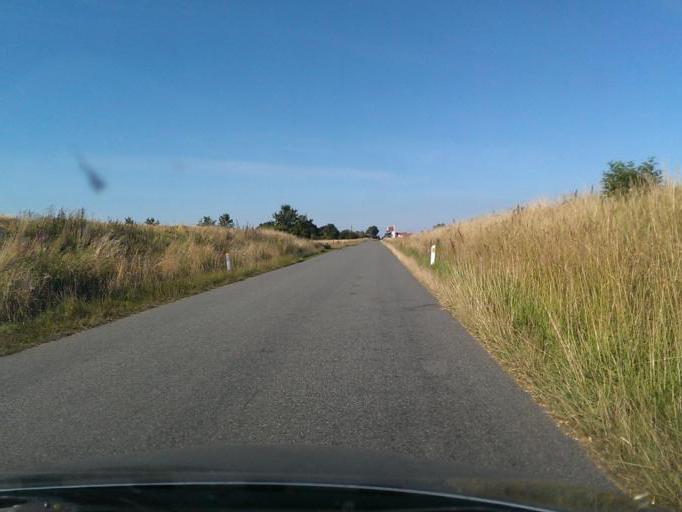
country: DK
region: Central Jutland
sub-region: Odder Kommune
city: Odder
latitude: 55.9034
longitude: 10.1349
